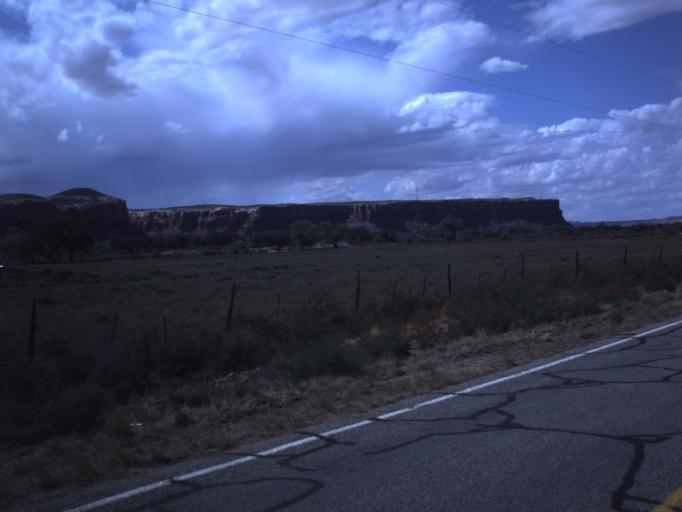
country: US
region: Utah
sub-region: San Juan County
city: Blanding
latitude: 37.2847
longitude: -109.5280
